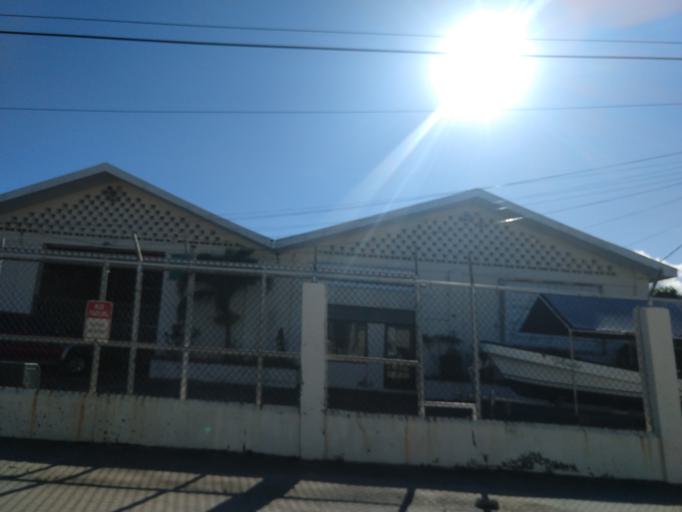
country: BZ
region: Belize
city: Belize City
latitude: 17.5062
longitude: -88.2020
